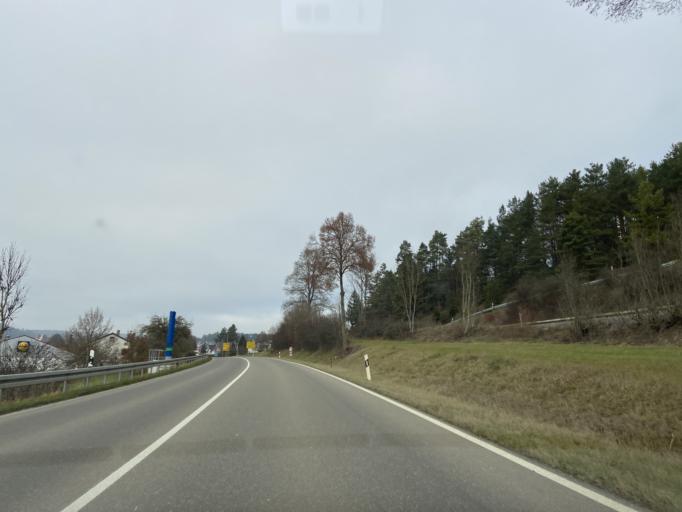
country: DE
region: Baden-Wuerttemberg
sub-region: Tuebingen Region
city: Gammertingen
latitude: 48.2433
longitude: 9.2257
